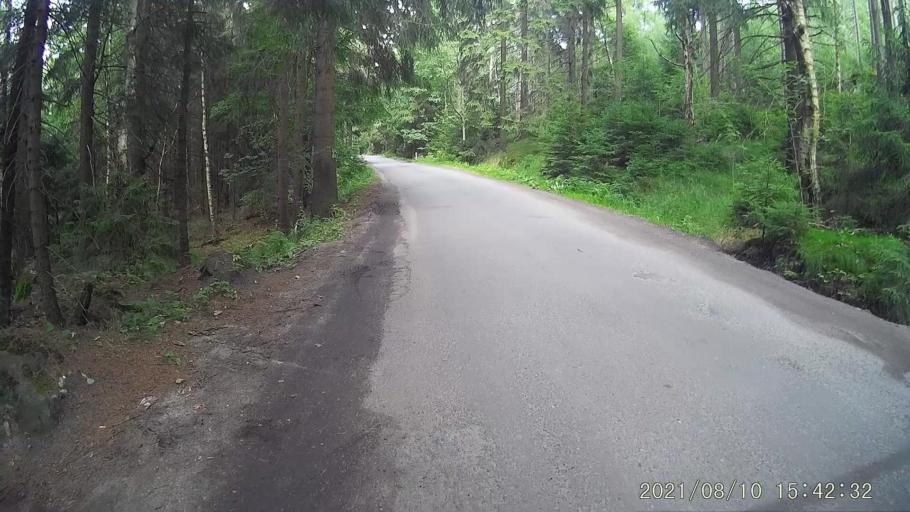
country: CZ
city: Machov
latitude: 50.4864
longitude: 16.3356
